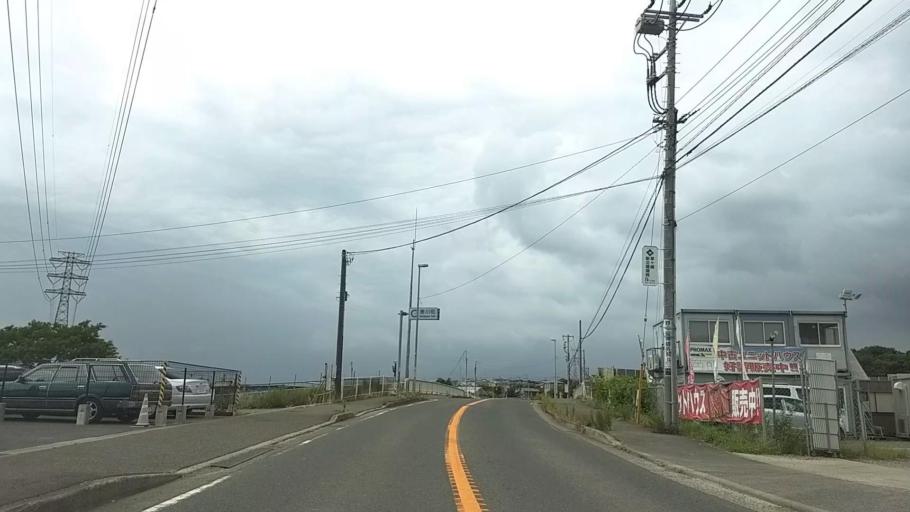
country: JP
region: Kanagawa
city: Chigasaki
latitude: 35.3680
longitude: 139.4017
